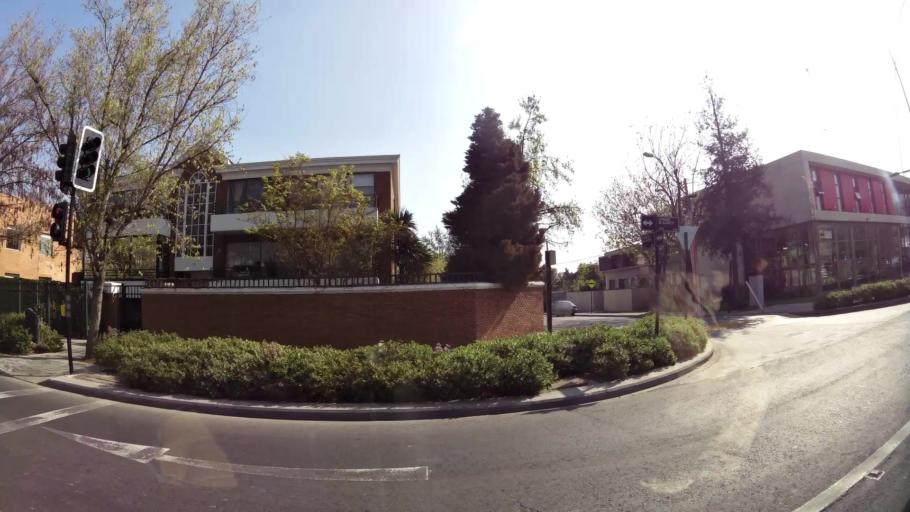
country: CL
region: Santiago Metropolitan
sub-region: Provincia de Santiago
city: Villa Presidente Frei, Nunoa, Santiago, Chile
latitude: -33.3927
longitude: -70.5625
